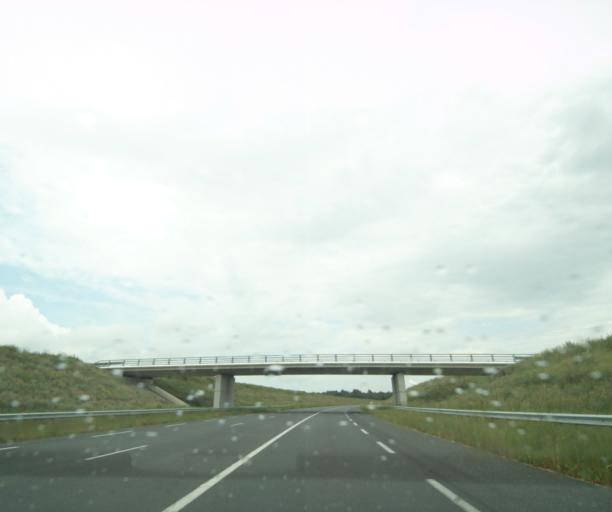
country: FR
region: Poitou-Charentes
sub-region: Departement des Deux-Sevres
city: Louzy
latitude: 47.0547
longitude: -0.1943
